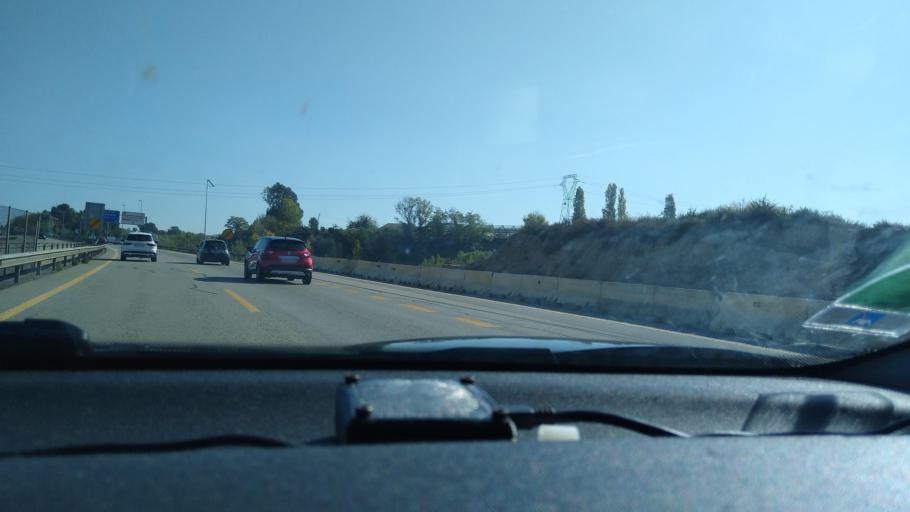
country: ES
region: Catalonia
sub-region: Provincia de Barcelona
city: Viladecavalls
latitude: 41.5548
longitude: 1.9806
